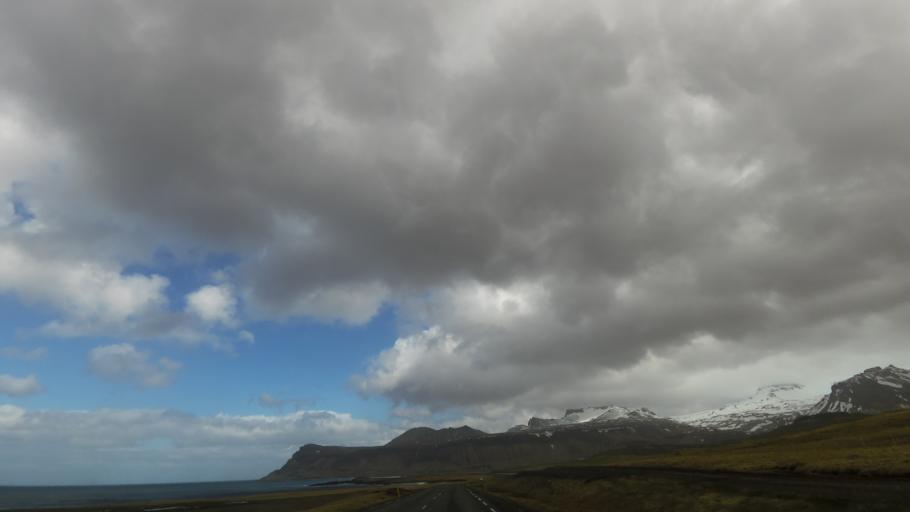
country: IS
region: West
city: Olafsvik
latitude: 64.9080
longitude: -23.5582
